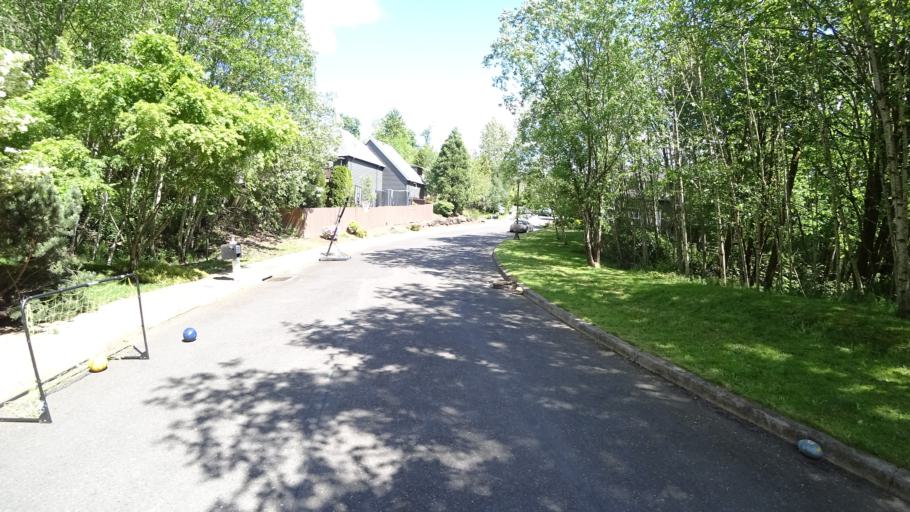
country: US
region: Oregon
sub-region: Washington County
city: West Haven
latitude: 45.5478
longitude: -122.7783
